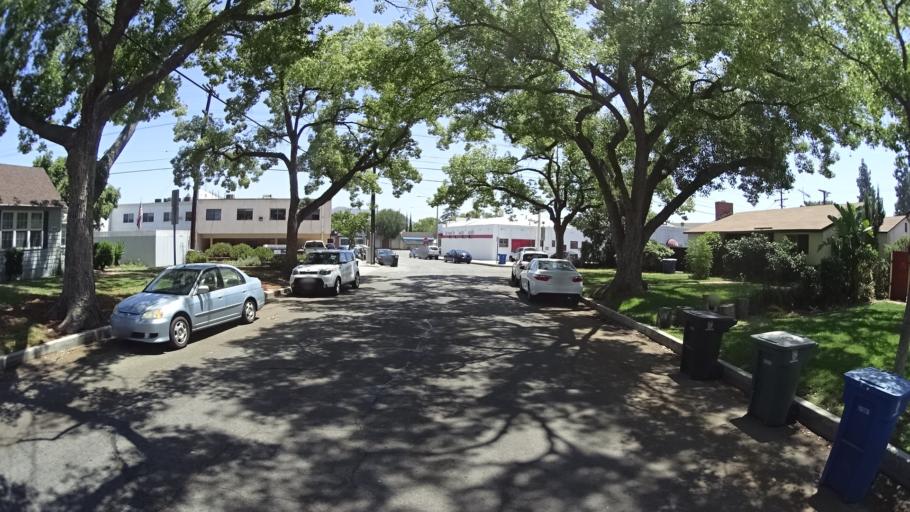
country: US
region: California
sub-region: Los Angeles County
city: Burbank
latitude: 34.1784
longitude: -118.3418
